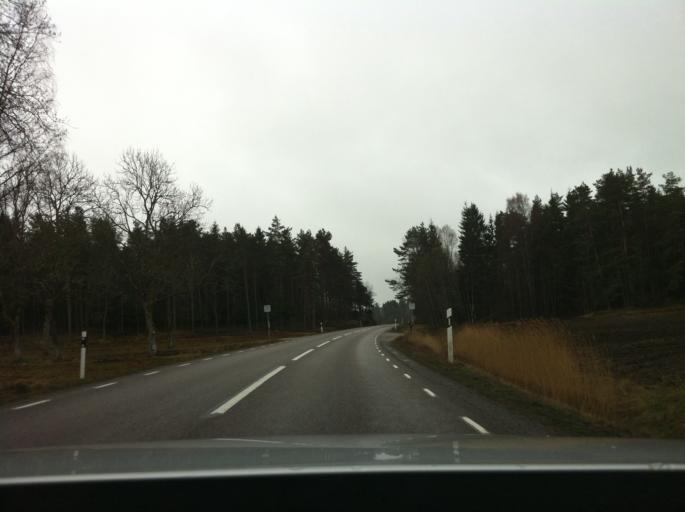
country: SE
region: Vaestra Goetaland
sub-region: Vanersborgs Kommun
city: Vargon
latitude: 58.2268
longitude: 12.4245
